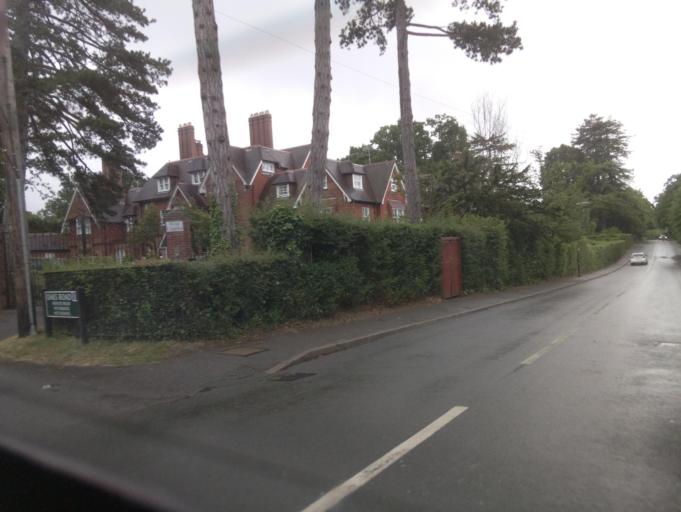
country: GB
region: England
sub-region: Surrey
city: Redhill
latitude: 51.2440
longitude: -0.1894
